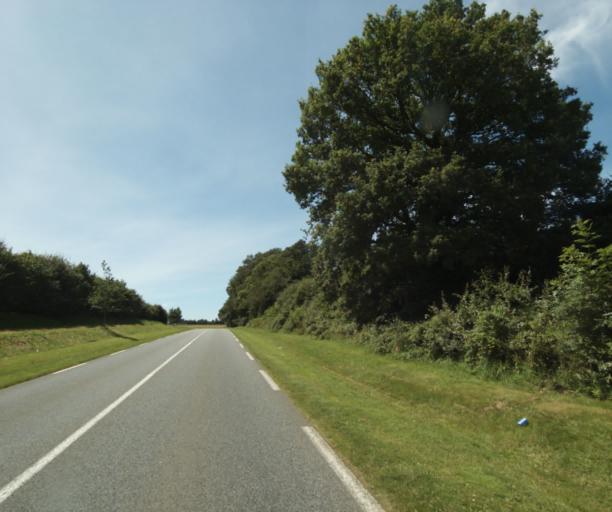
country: FR
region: Pays de la Loire
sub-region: Departement de la Mayenne
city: Saint-Berthevin
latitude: 48.0782
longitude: -0.8124
